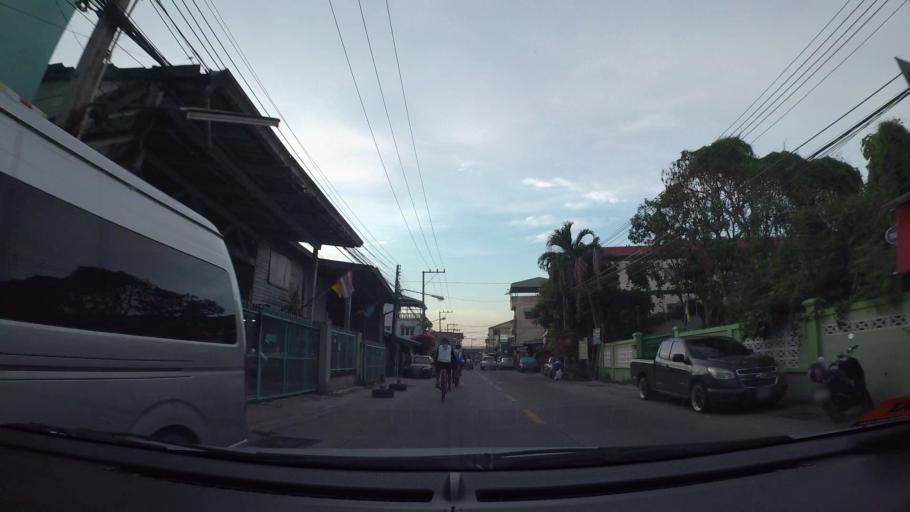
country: TH
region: Chon Buri
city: Chon Buri
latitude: 13.3938
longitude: 100.9859
